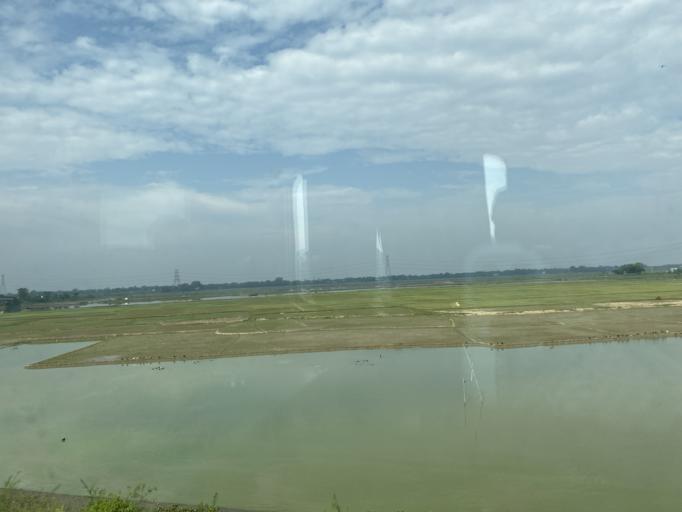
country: IN
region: Tripura
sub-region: West Tripura
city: Agartala
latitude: 23.8812
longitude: 91.2045
